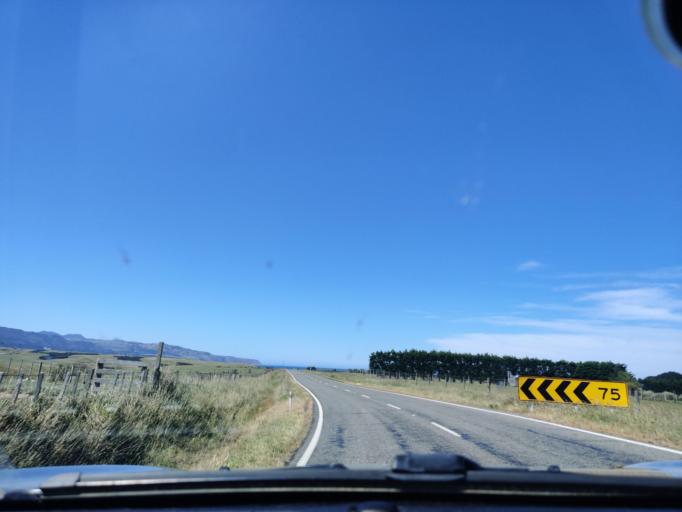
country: NZ
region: Wellington
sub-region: Upper Hutt City
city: Upper Hutt
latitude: -41.3895
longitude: 175.1758
